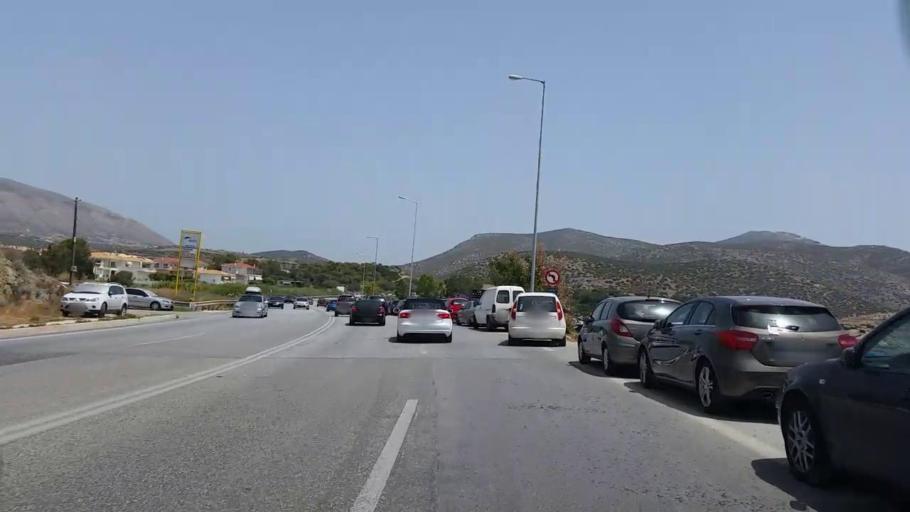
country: GR
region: Attica
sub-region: Nomarchia Anatolikis Attikis
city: Saronida
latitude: 37.7788
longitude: 23.8942
